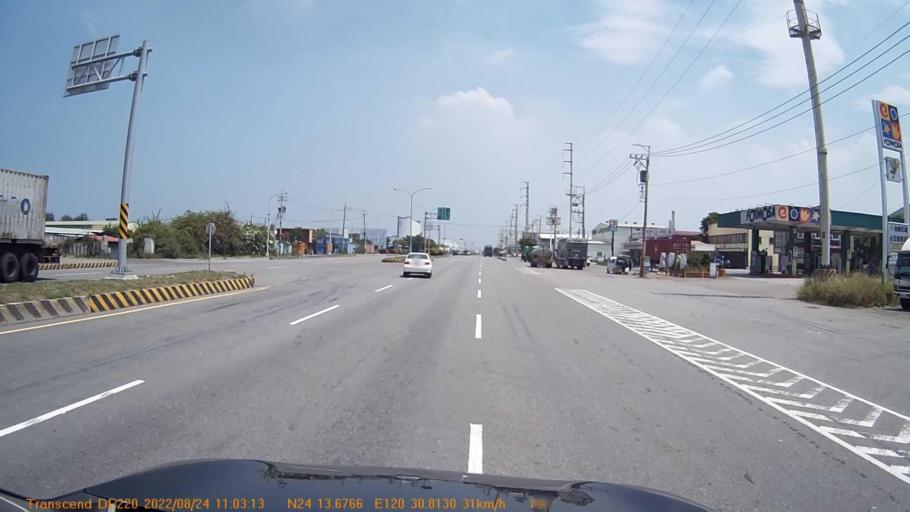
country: TW
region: Taiwan
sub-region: Changhua
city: Chang-hua
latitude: 24.2282
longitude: 120.5136
